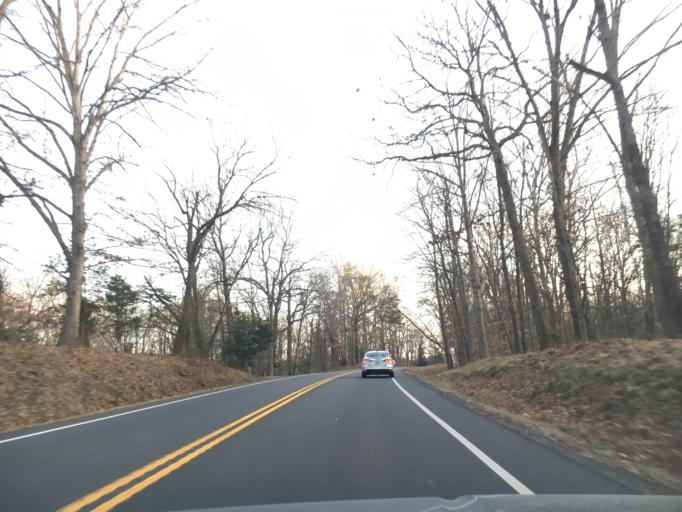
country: US
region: Virginia
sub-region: Culpeper County
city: Culpeper
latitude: 38.3444
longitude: -77.9564
